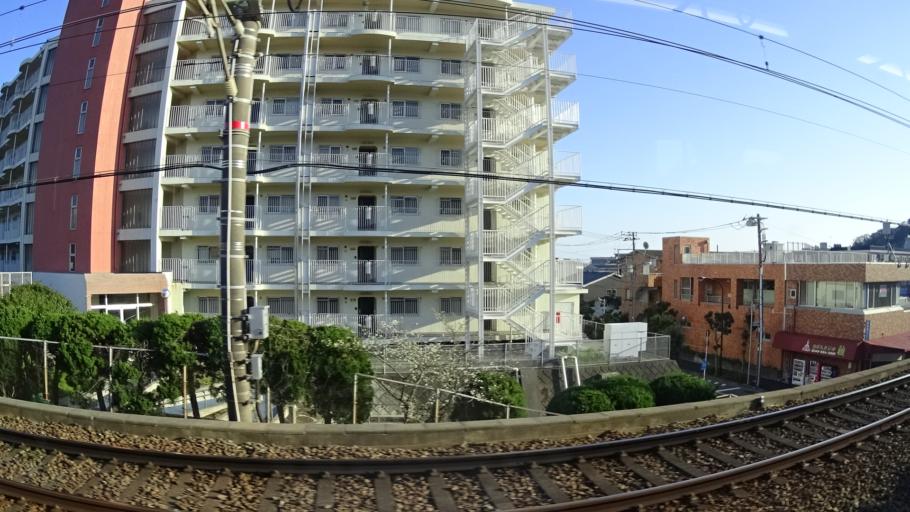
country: JP
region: Kanagawa
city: Yokosuka
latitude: 35.2059
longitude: 139.6749
